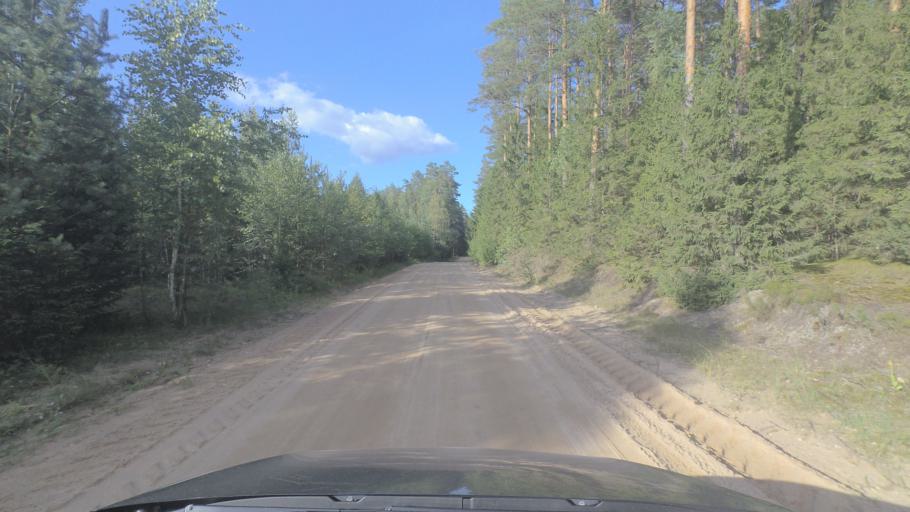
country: LT
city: Pabrade
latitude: 55.1630
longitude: 25.8282
